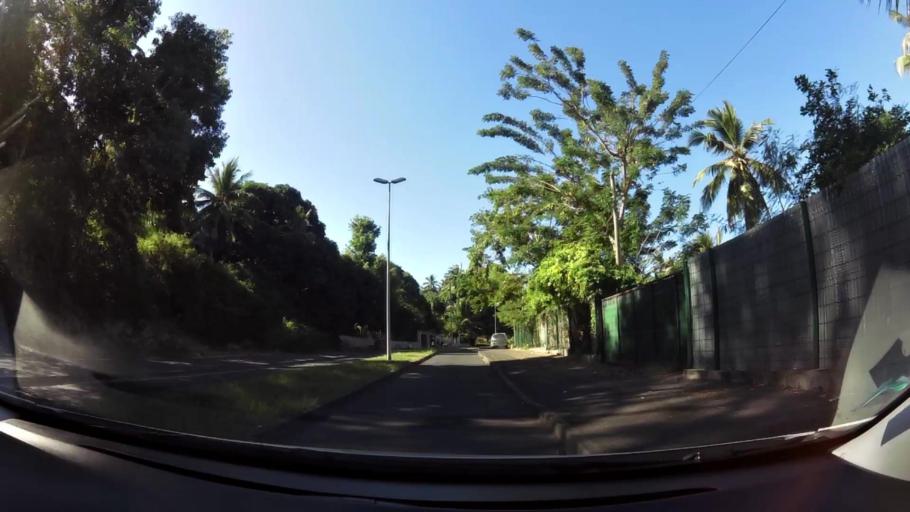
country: YT
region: Pamandzi
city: Pamandzi
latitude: -12.7931
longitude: 45.2776
